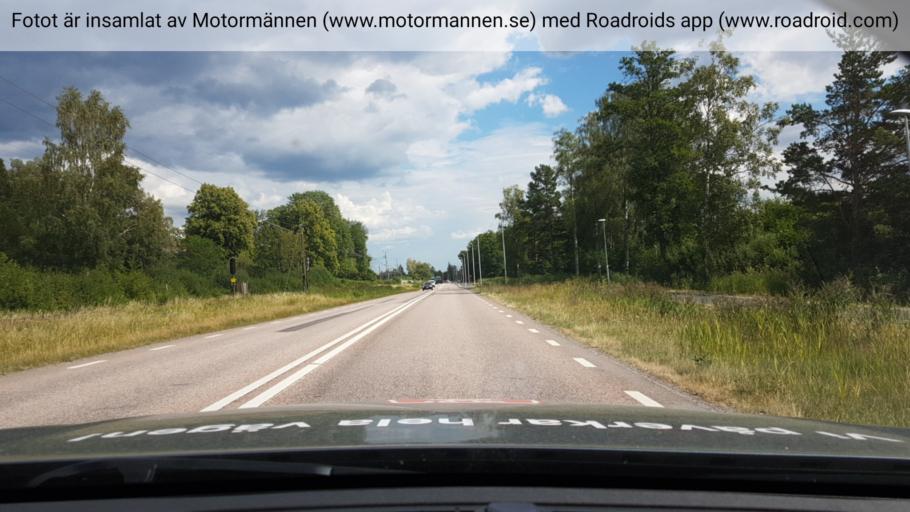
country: SE
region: Uppsala
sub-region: Heby Kommun
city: Morgongava
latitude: 59.9359
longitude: 16.9485
